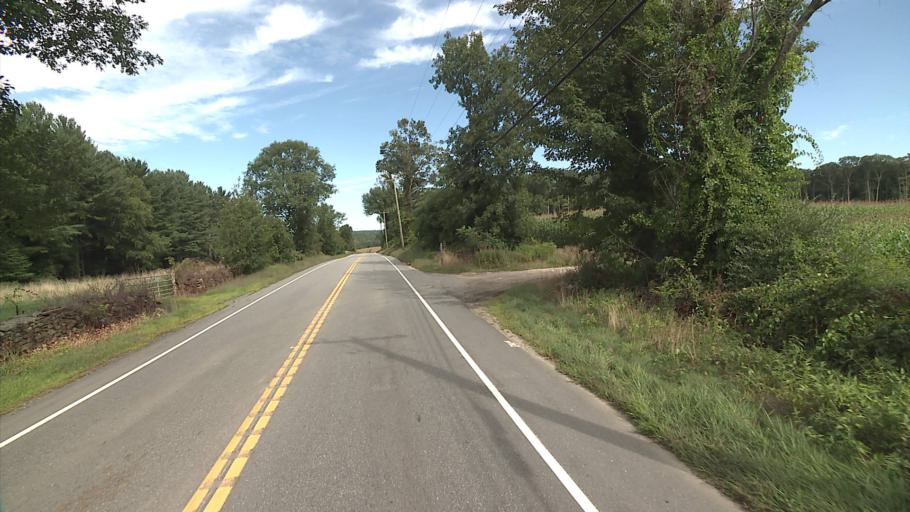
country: US
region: Connecticut
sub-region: Tolland County
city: South Coventry
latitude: 41.8120
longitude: -72.3075
